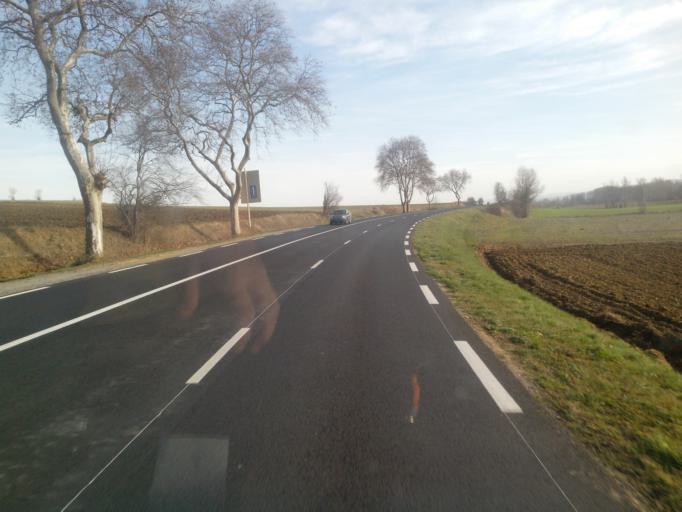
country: FR
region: Languedoc-Roussillon
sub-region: Departement de l'Aude
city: Villepinte
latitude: 43.2779
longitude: 2.0967
